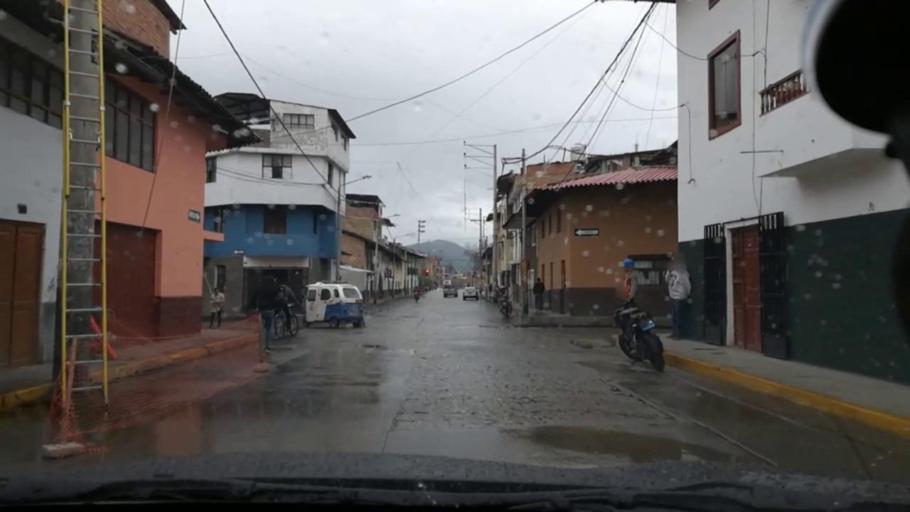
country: PE
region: Cajamarca
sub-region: Provincia de Cajamarca
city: Cajamarca
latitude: -7.1583
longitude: -78.5122
